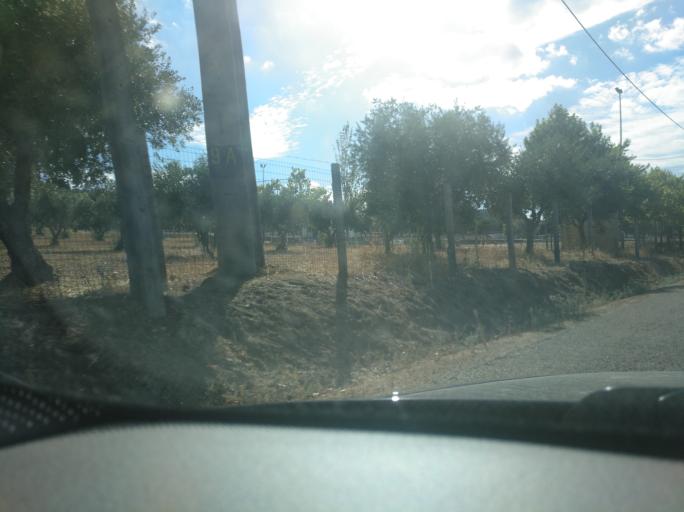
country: ES
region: Extremadura
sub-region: Provincia de Badajoz
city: La Codosera
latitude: 39.1584
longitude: -7.1857
